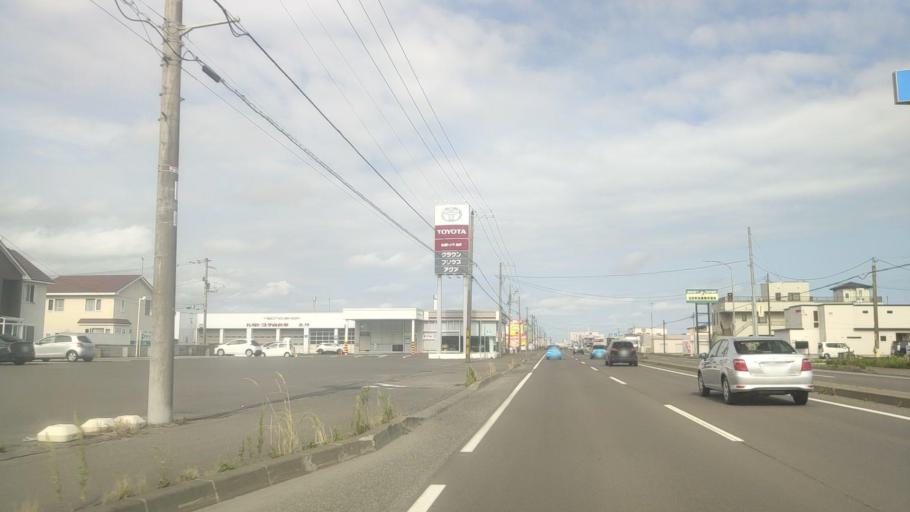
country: JP
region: Hokkaido
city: Tomakomai
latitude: 42.6173
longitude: 141.5425
